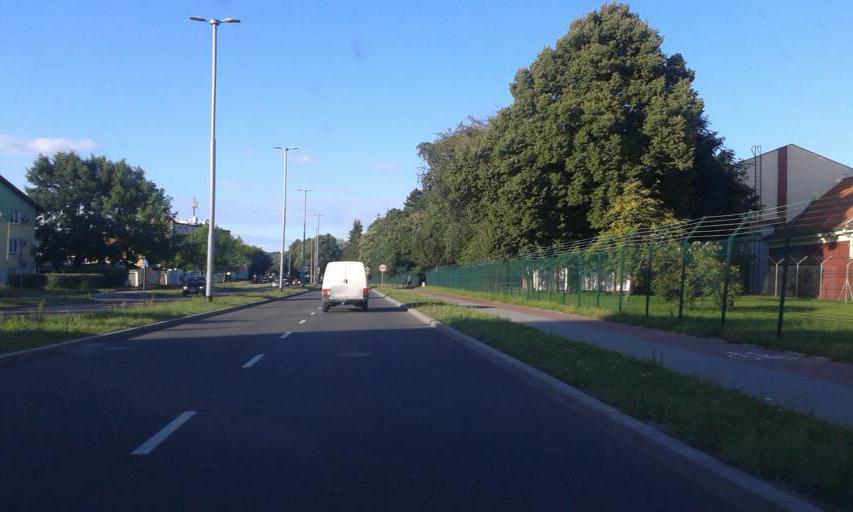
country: PL
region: West Pomeranian Voivodeship
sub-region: Koszalin
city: Koszalin
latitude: 54.1831
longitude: 16.2032
